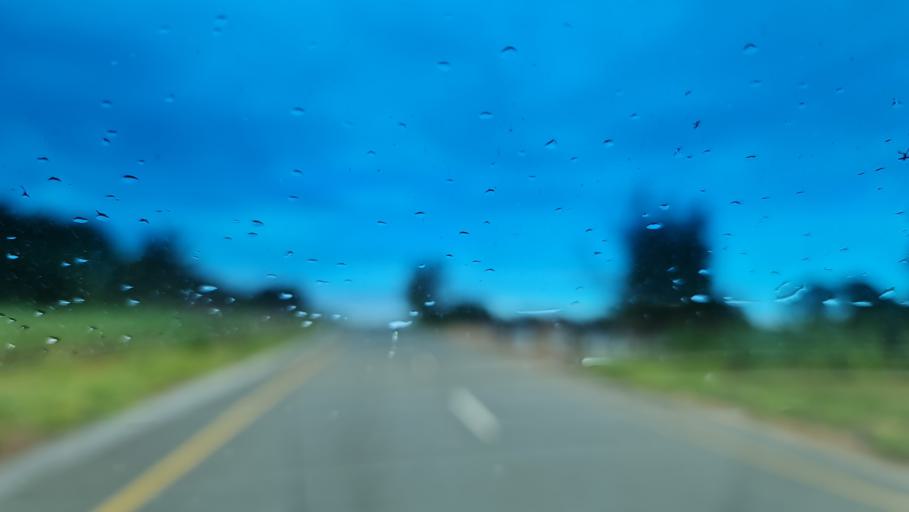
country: MZ
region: Nampula
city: Nampula
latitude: -15.5440
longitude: 39.3255
